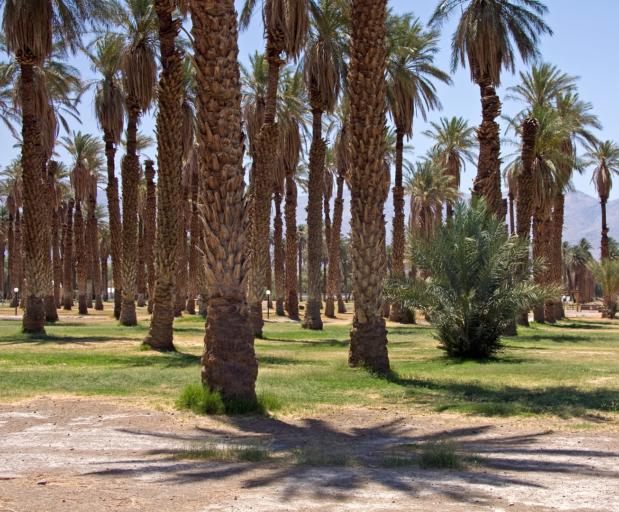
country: US
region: Nevada
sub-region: Nye County
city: Beatty
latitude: 36.4590
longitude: -116.8657
